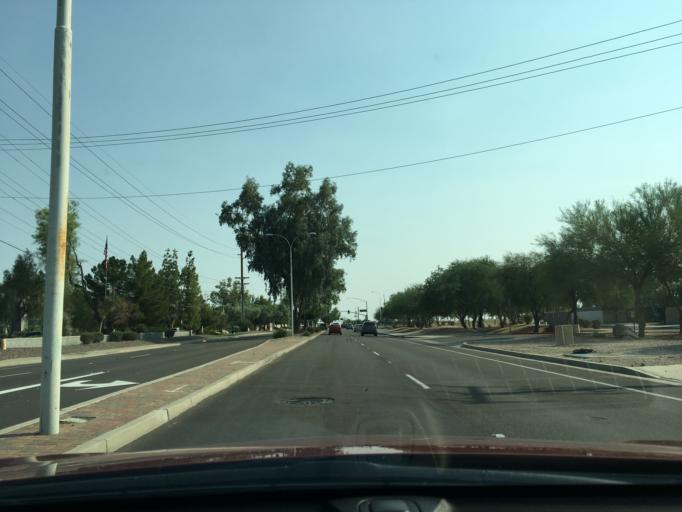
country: US
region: Arizona
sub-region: Maricopa County
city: Guadalupe
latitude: 33.2984
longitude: -111.9457
